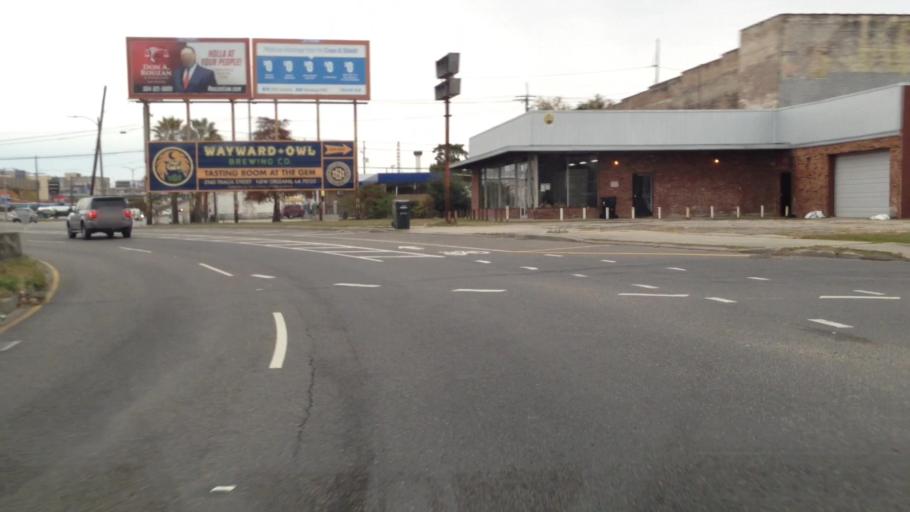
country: US
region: Louisiana
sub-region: Orleans Parish
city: New Orleans
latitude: 29.9518
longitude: -90.0982
